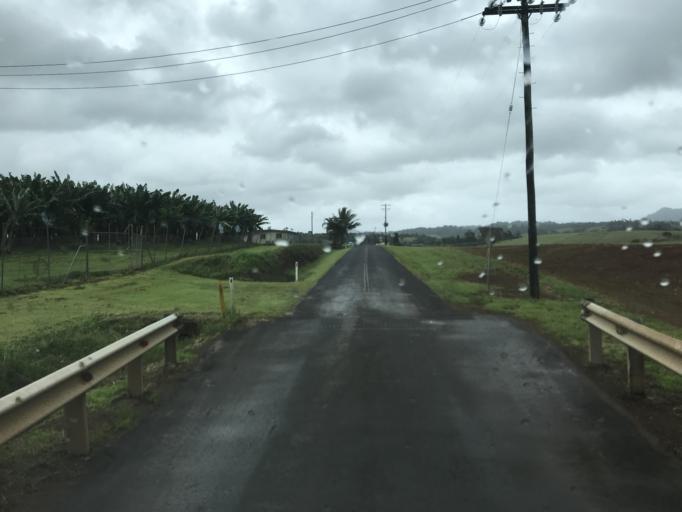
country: AU
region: Queensland
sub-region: Cassowary Coast
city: Innisfail
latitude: -17.5192
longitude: 145.9682
